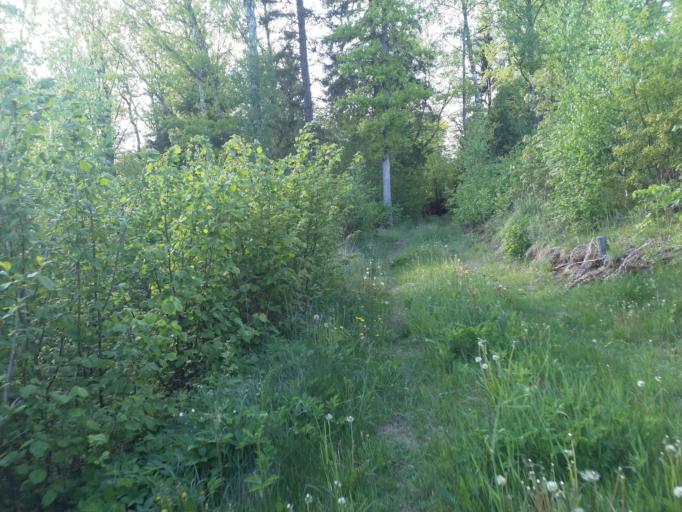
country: LV
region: Kuldigas Rajons
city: Kuldiga
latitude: 56.8546
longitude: 21.8685
